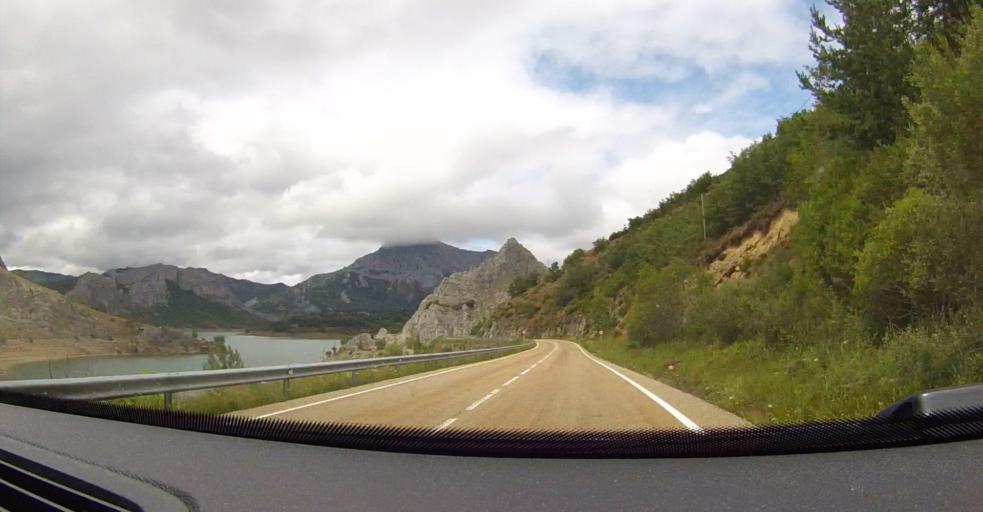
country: ES
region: Castille and Leon
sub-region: Provincia de Leon
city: Reyero
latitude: 42.9563
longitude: -5.2501
